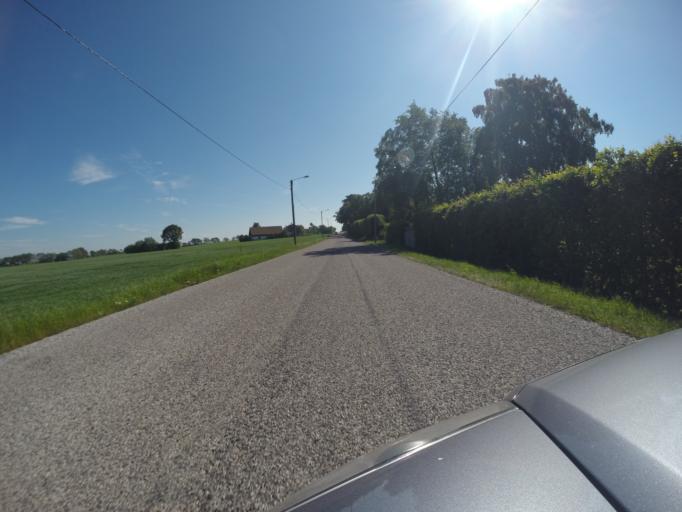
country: SE
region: Skane
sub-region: Helsingborg
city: Morarp
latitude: 56.0249
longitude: 12.8685
